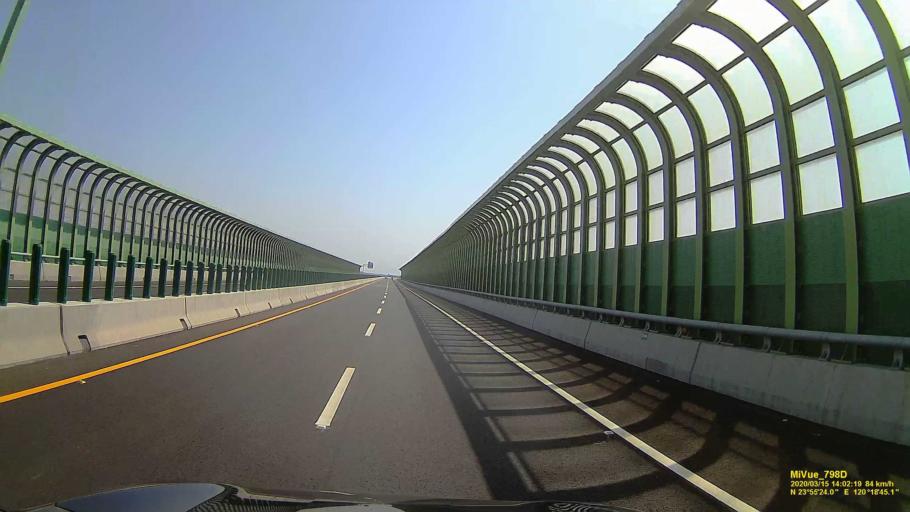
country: TW
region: Taiwan
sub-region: Changhua
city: Chang-hua
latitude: 23.9230
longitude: 120.3126
